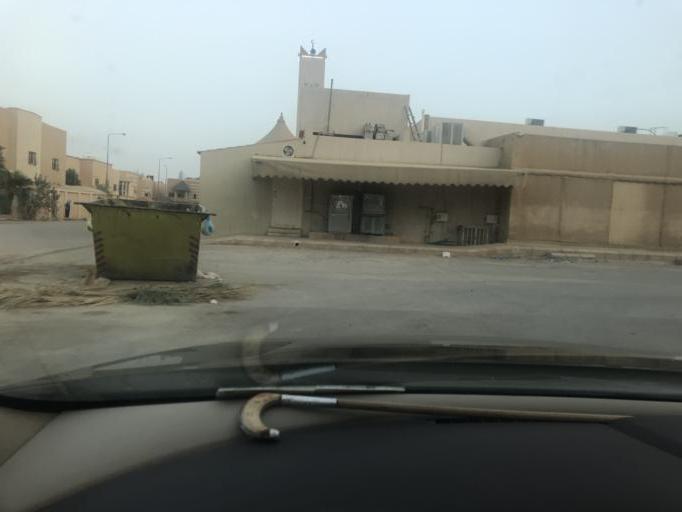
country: SA
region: Ar Riyad
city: Riyadh
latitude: 24.7305
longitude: 46.7464
